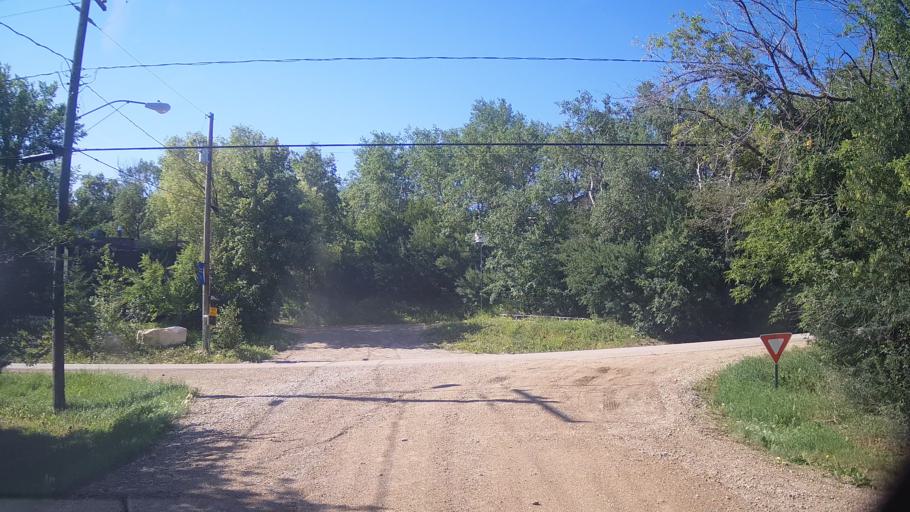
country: CA
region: Saskatchewan
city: Watrous
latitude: 51.7199
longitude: -105.4490
